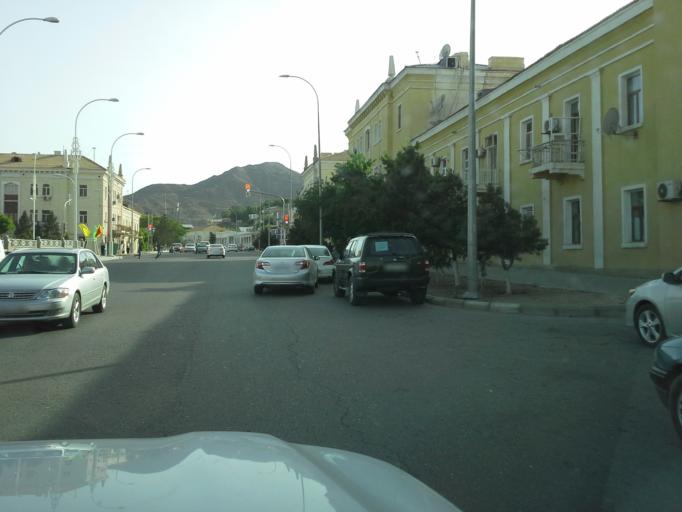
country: TM
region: Balkan
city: Turkmenbasy
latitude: 40.0058
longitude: 52.9932
